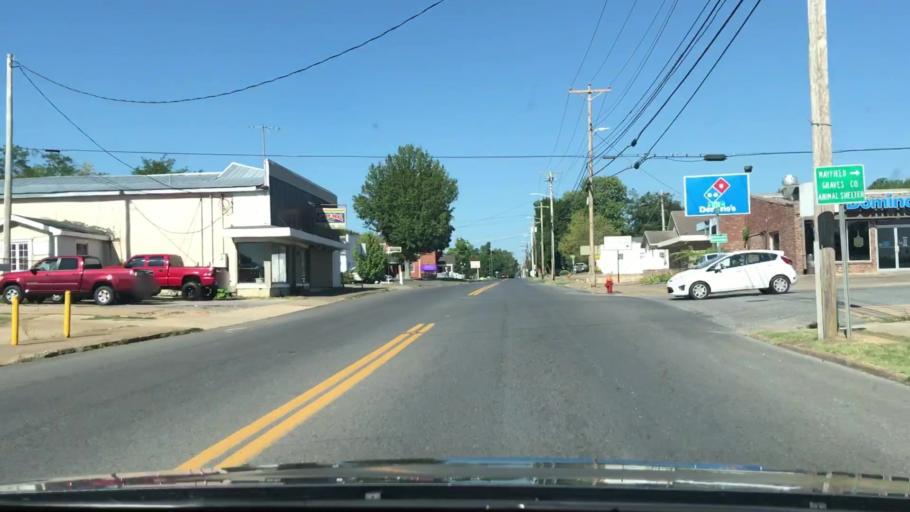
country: US
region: Kentucky
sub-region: Graves County
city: Mayfield
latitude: 36.7417
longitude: -88.6421
